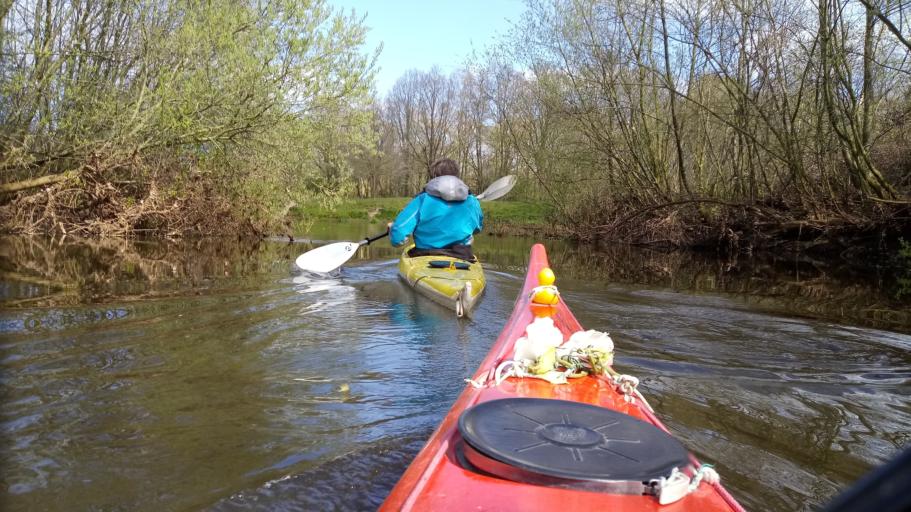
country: NL
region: Overijssel
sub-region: Gemeente Twenterand
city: Den Ham
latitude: 52.4487
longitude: 6.4405
